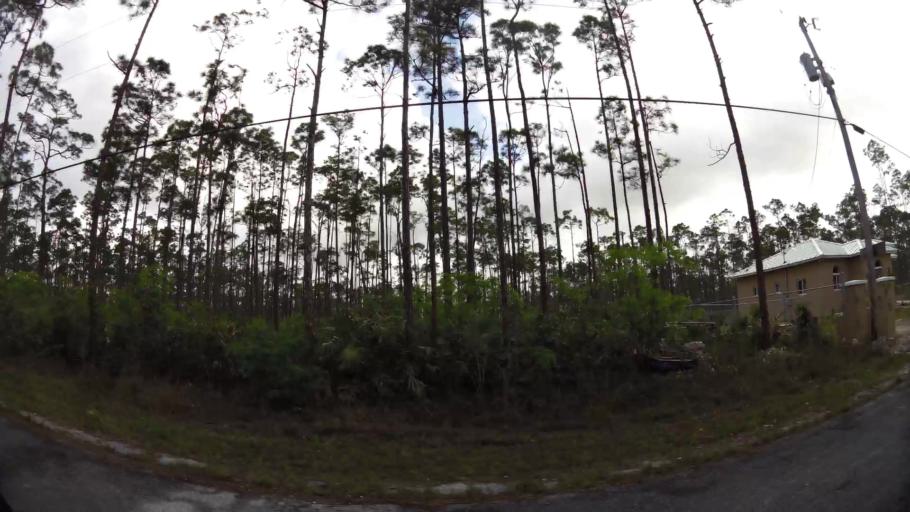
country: BS
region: Freeport
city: Lucaya
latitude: 26.5885
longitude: -78.5487
